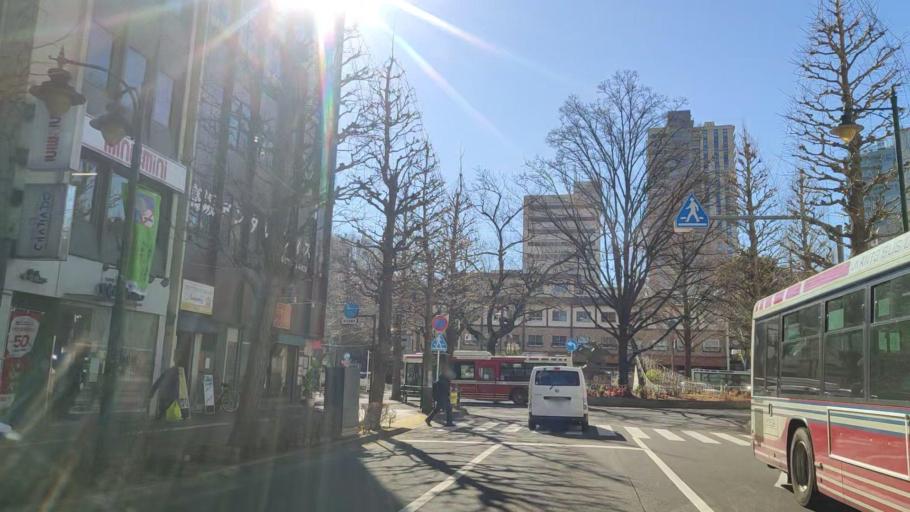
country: JP
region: Tokyo
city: Musashino
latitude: 35.7040
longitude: 139.5606
